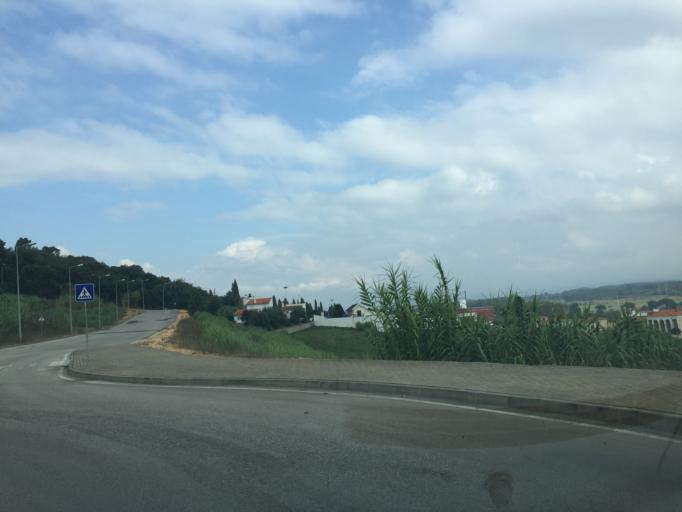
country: PT
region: Aveiro
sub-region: Anadia
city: Arcos
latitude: 40.4424
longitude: -8.4406
